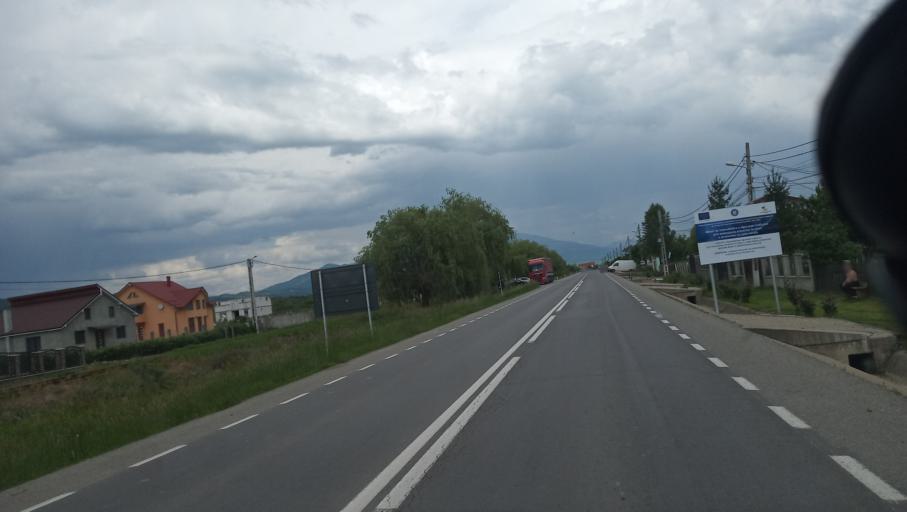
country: RO
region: Bistrita-Nasaud
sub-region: Comuna Livezile
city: Livezile
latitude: 47.1848
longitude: 24.5942
